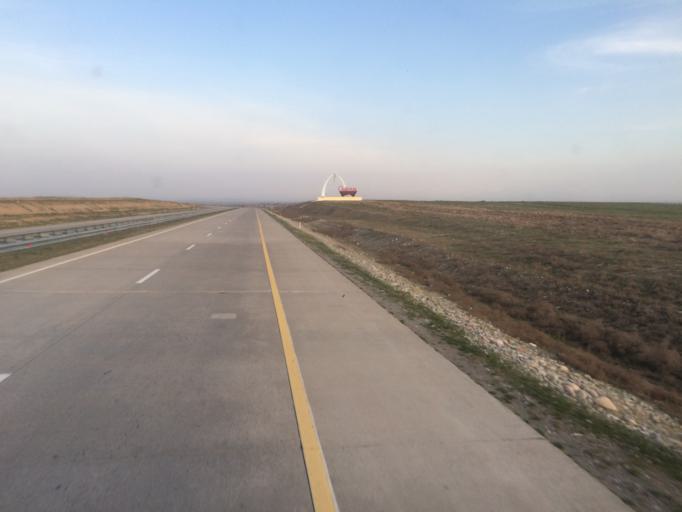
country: KZ
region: Ongtustik Qazaqstan
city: Shymkent
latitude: 42.4937
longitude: 69.4750
